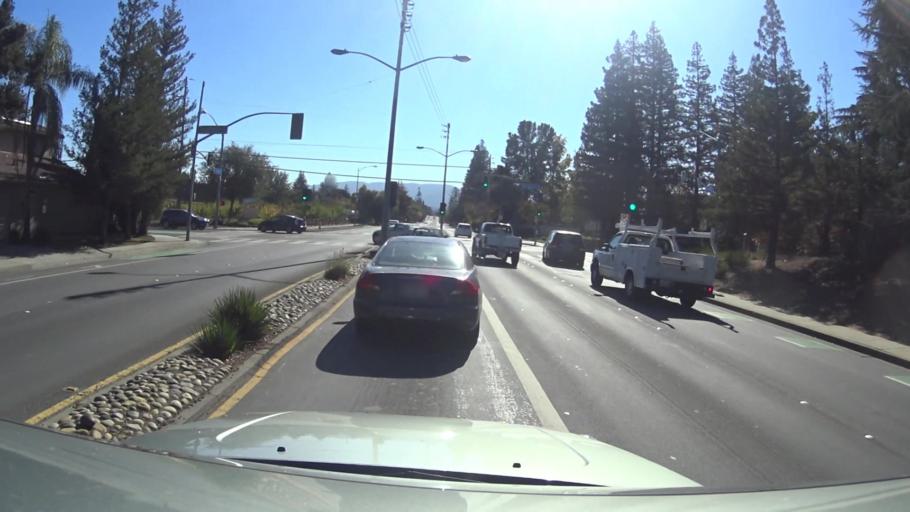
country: US
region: California
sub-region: Santa Clara County
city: Cupertino
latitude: 37.3160
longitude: -122.0415
